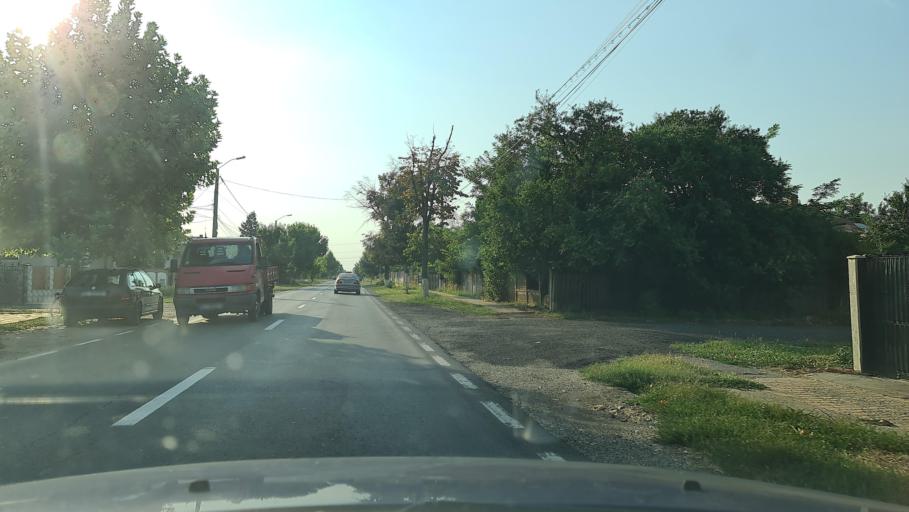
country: RO
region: Calarasi
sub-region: Comuna Dor Marunt
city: Dor Marunt
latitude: 44.4427
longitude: 26.9347
